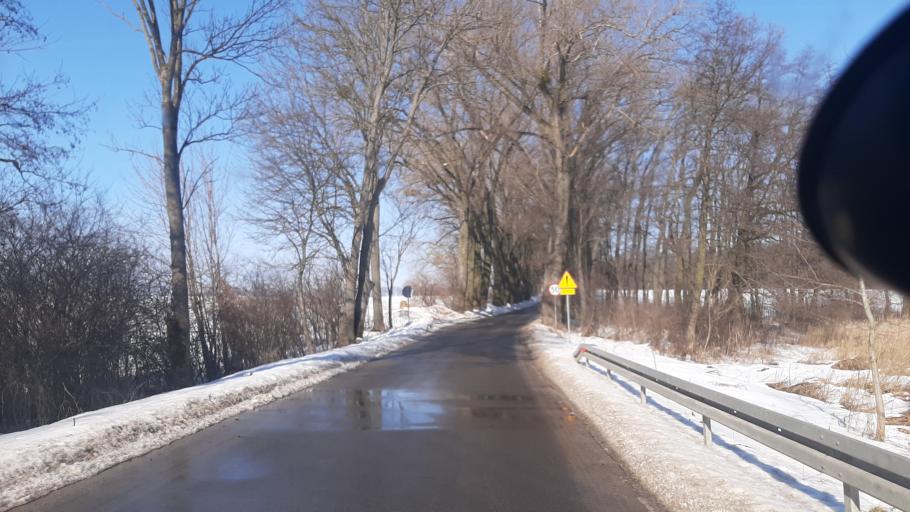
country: PL
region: Lublin Voivodeship
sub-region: Powiat pulawski
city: Naleczow
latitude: 51.2969
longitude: 22.2637
